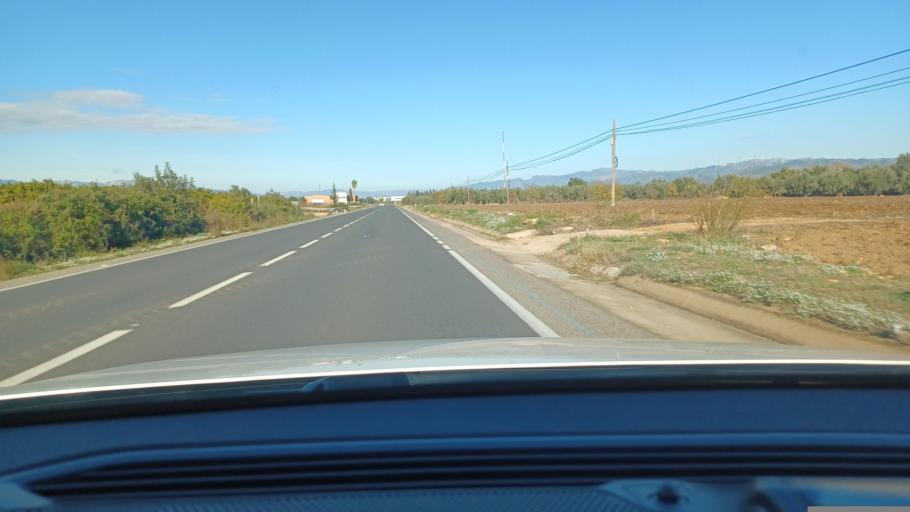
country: ES
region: Catalonia
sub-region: Provincia de Tarragona
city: Santa Barbara
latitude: 40.7279
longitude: 0.5033
